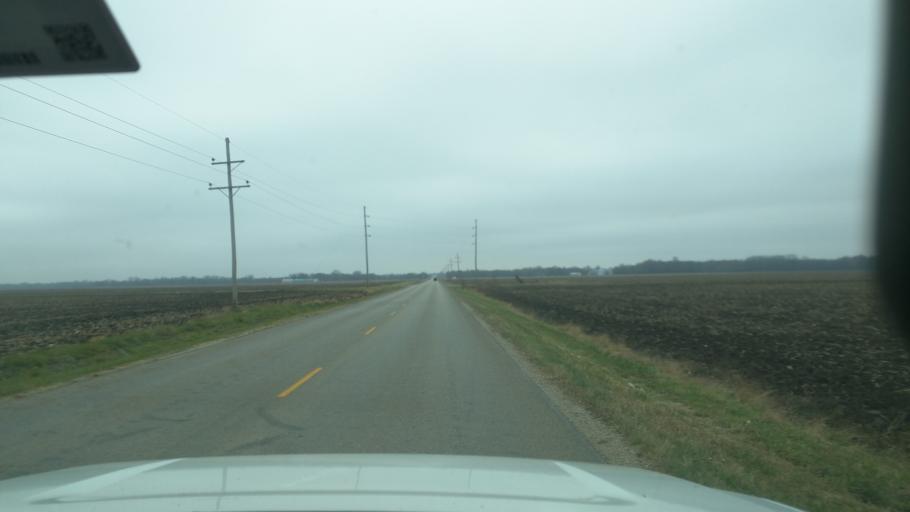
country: US
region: Kansas
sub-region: Lyon County
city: Emporia
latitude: 38.4866
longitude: -96.2529
